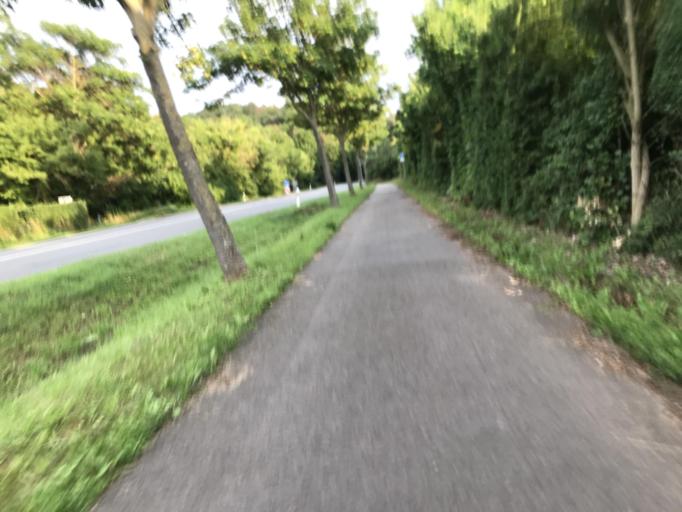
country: DE
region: Saxony-Anhalt
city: Quedlinburg
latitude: 51.8038
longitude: 11.1310
